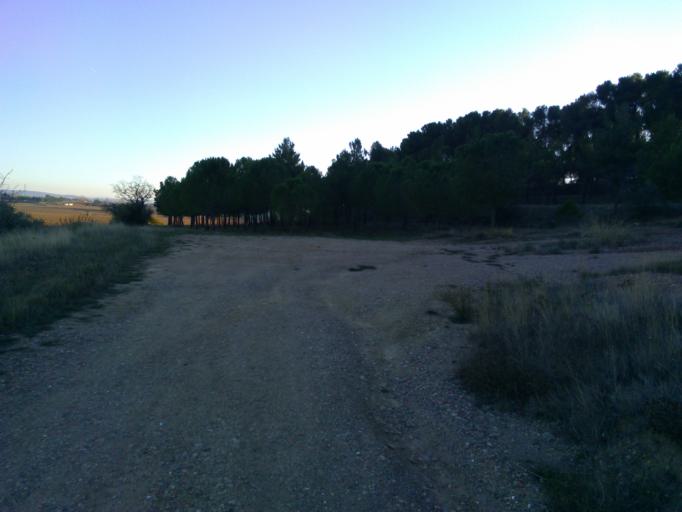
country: FR
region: Languedoc-Roussillon
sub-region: Departement de l'Aude
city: Pepieux
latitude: 43.3135
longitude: 2.6807
